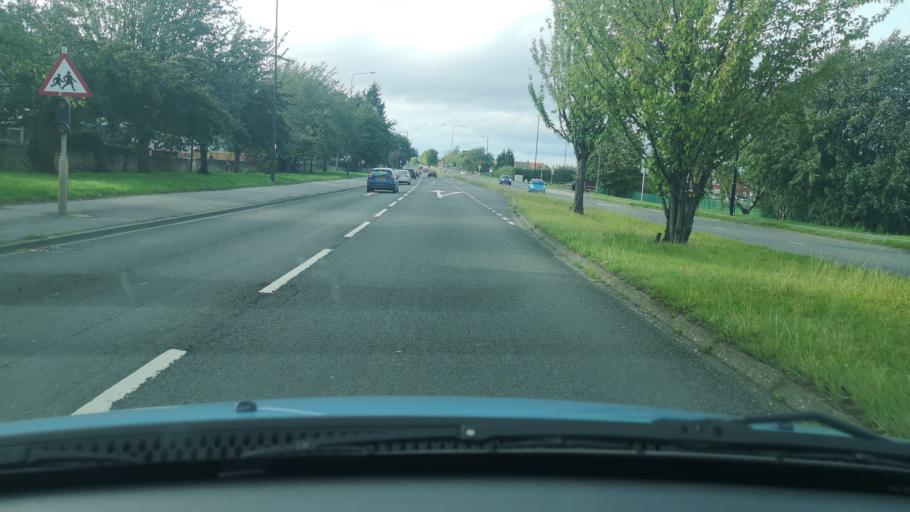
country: GB
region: England
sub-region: Doncaster
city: Carcroft
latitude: 53.5661
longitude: -1.1969
